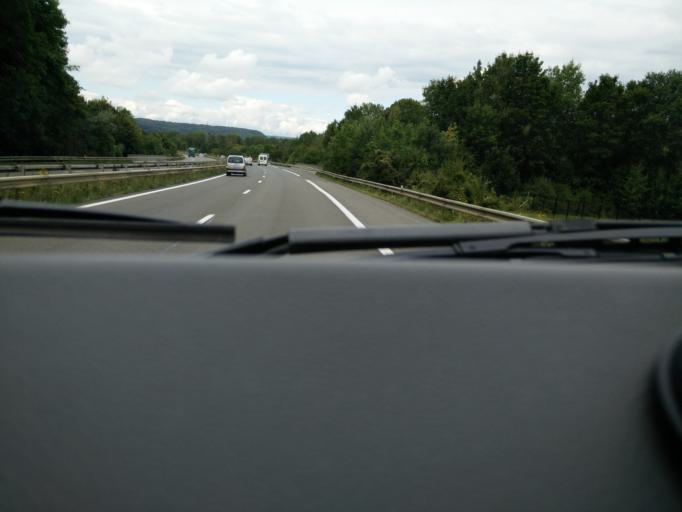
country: FR
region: Champagne-Ardenne
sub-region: Departement des Ardennes
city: Donchery
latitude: 49.7027
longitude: 4.9033
